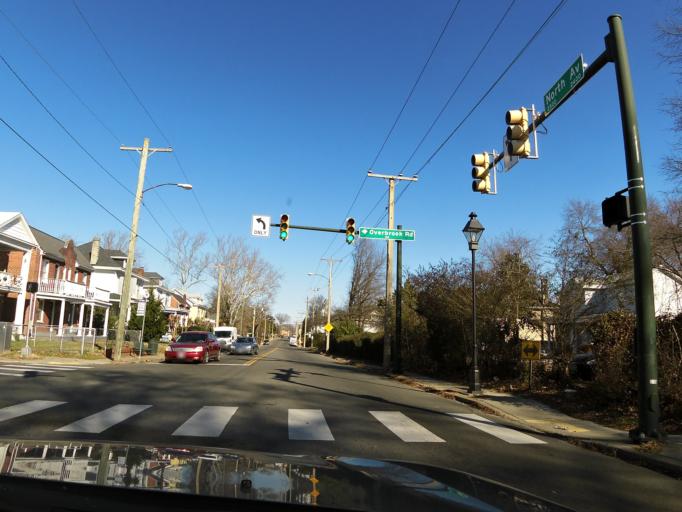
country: US
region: Virginia
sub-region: City of Richmond
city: Richmond
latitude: 37.5648
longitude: -77.4332
